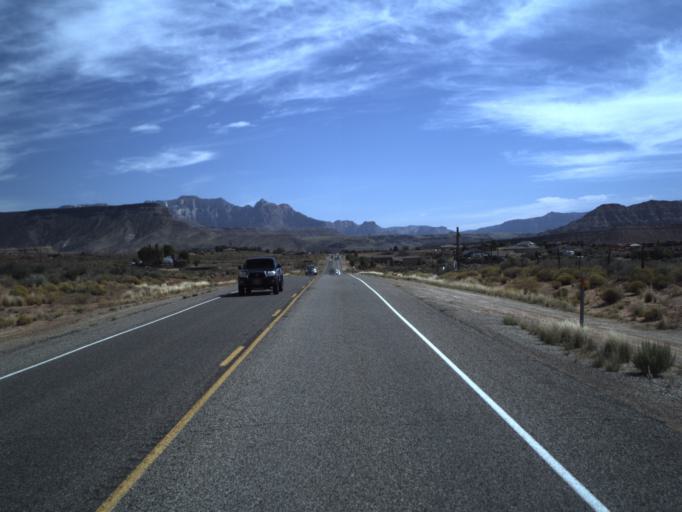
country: US
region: Utah
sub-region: Washington County
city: LaVerkin
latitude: 37.2069
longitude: -113.2247
